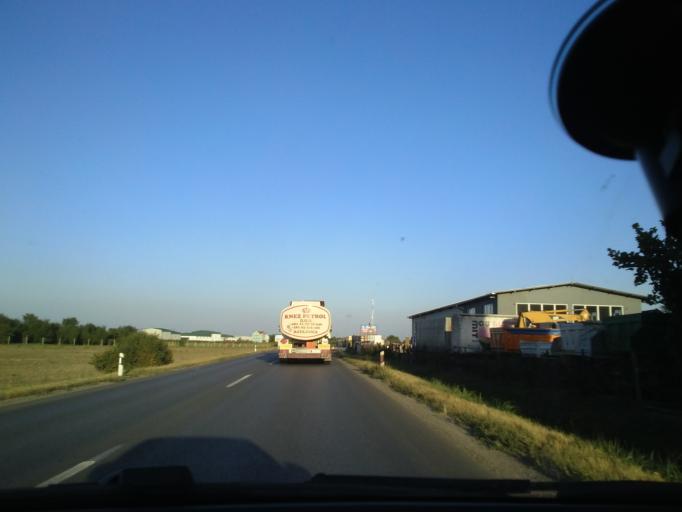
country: RS
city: Rumenka
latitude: 45.2873
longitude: 19.7571
